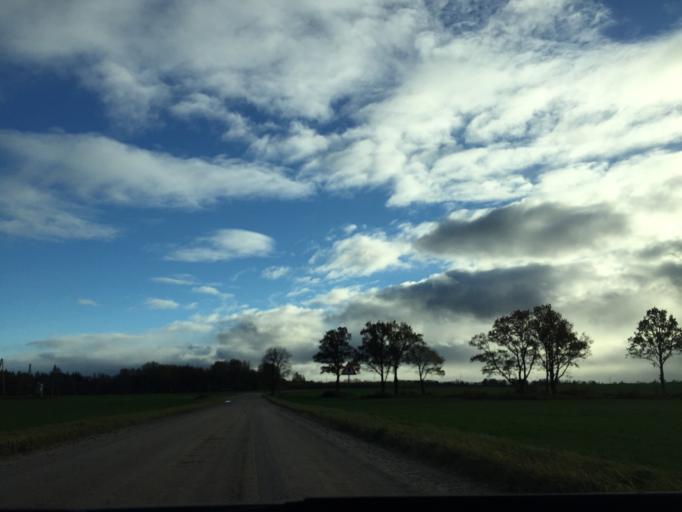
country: LV
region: Tukuma Rajons
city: Tukums
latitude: 56.9365
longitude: 22.9528
